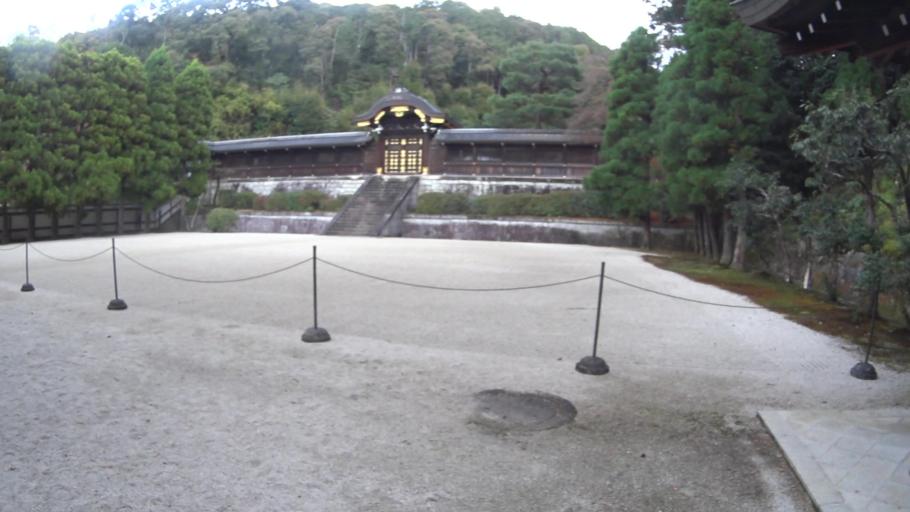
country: JP
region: Kyoto
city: Kyoto
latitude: 34.9771
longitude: 135.7811
